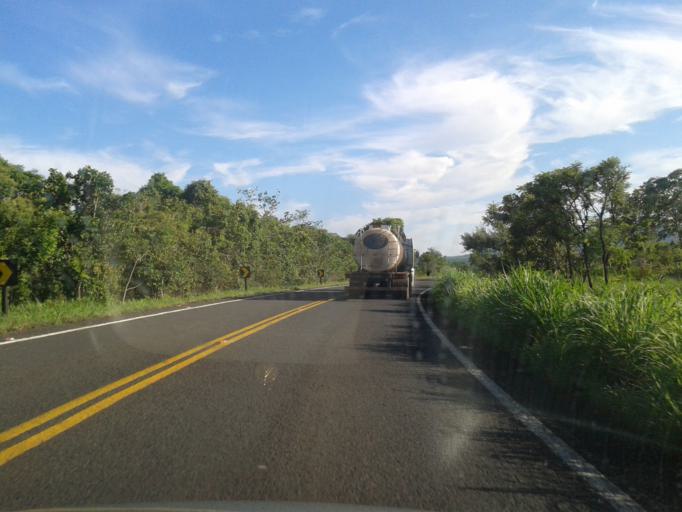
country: BR
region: Minas Gerais
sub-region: Tupaciguara
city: Tupaciguara
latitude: -18.2162
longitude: -48.5747
